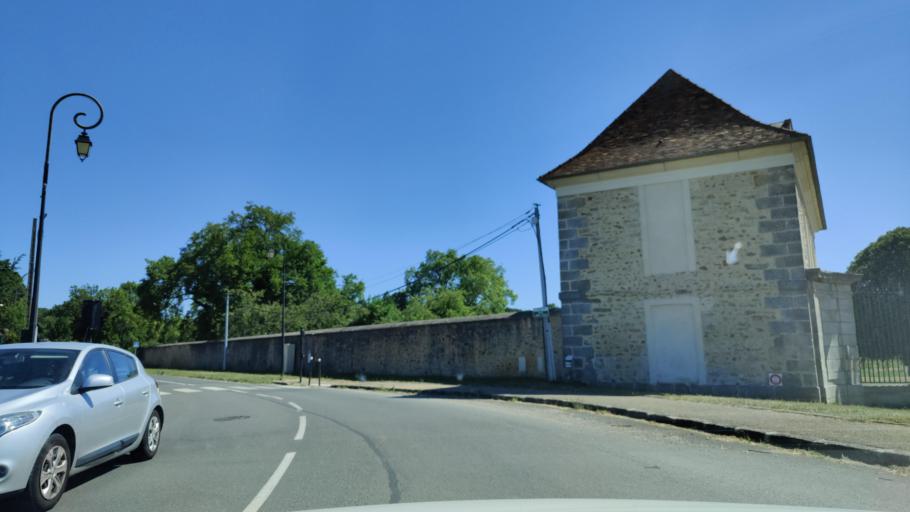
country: FR
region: Ile-de-France
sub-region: Departement de l'Essonne
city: Fontenay-les-Briis
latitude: 48.6089
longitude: 2.1656
